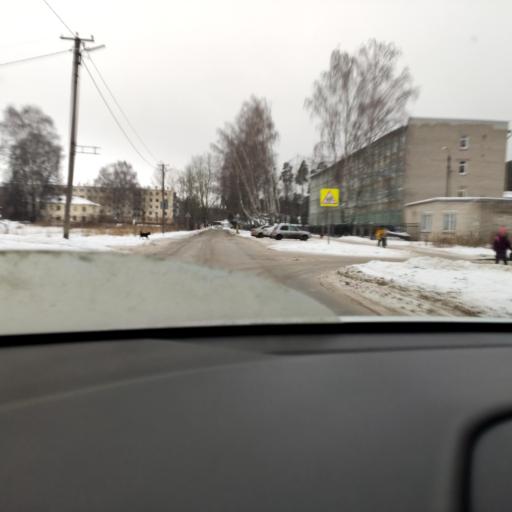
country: RU
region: Tatarstan
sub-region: Zelenodol'skiy Rayon
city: Zelenodolsk
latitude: 55.8544
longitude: 48.4858
